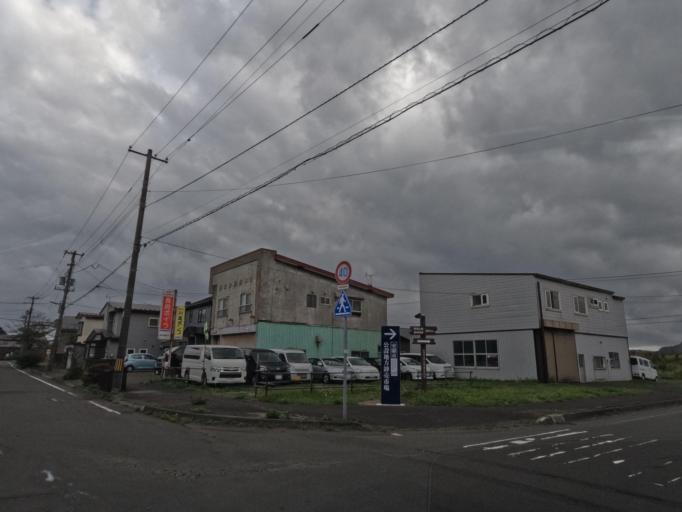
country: JP
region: Hokkaido
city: Muroran
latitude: 42.3393
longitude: 141.0304
